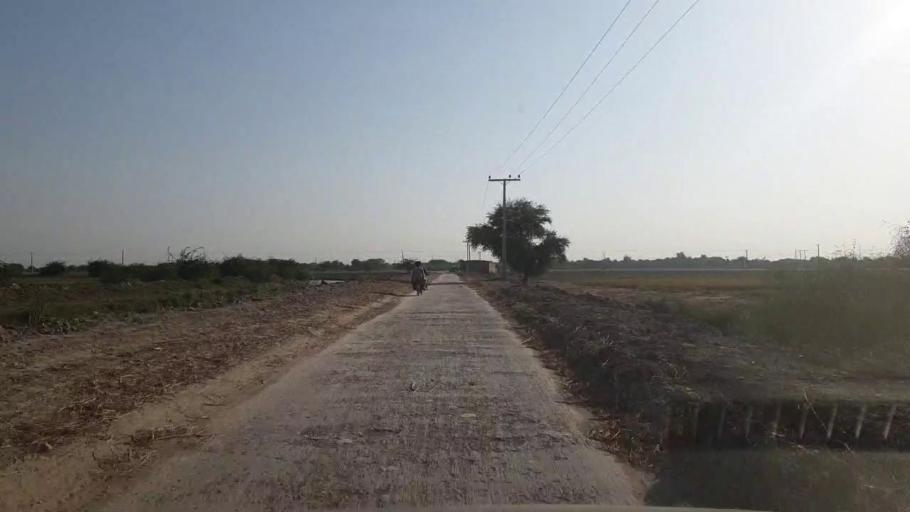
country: PK
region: Sindh
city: Talhar
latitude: 24.9092
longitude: 68.7426
